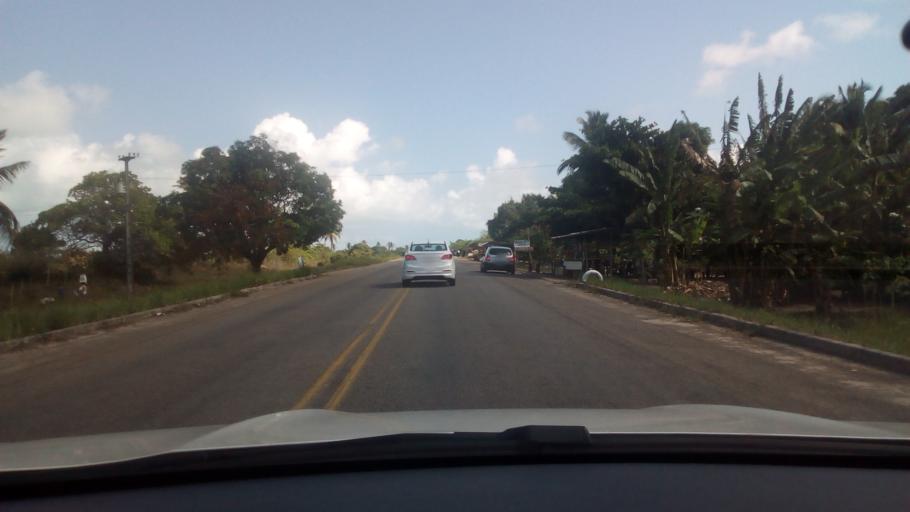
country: BR
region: Paraiba
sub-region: Conde
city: Conde
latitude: -7.2413
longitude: -34.8341
